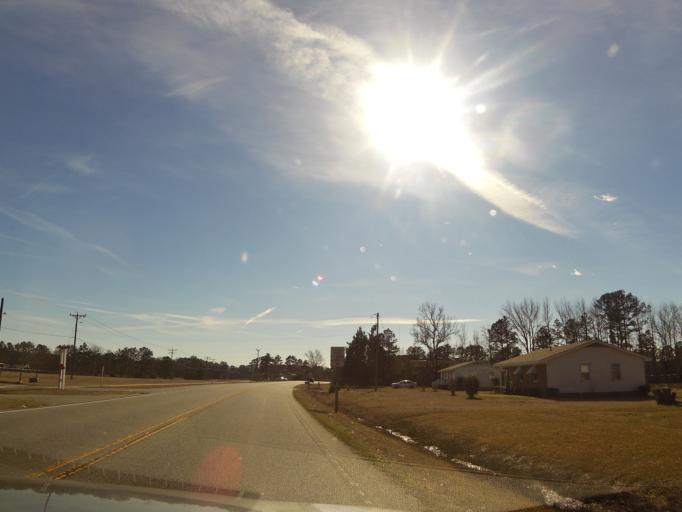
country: US
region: Virginia
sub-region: Isle of Wight County
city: Windsor
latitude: 36.8258
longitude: -76.7451
